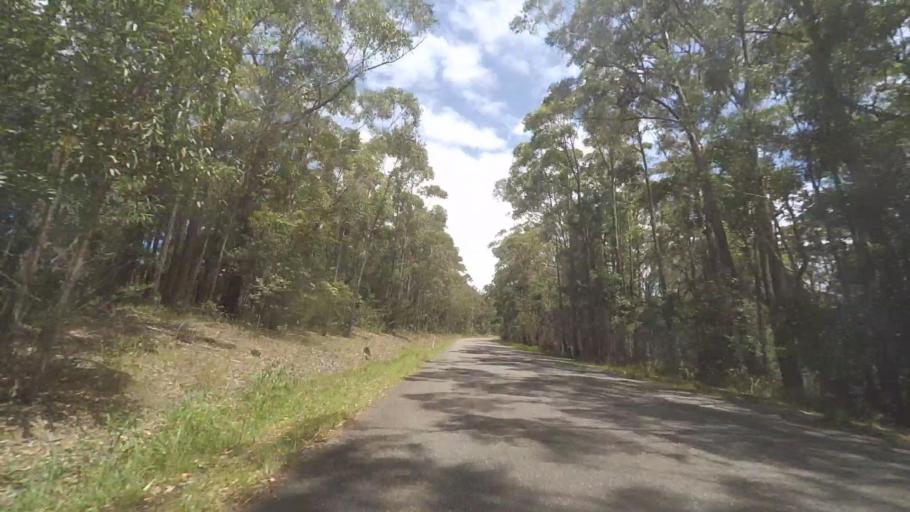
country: AU
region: New South Wales
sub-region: Shoalhaven Shire
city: Milton
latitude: -35.4004
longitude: 150.3656
